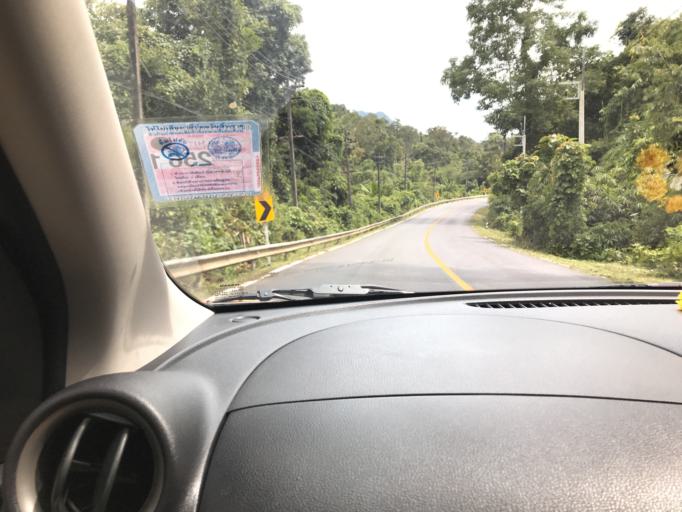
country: TH
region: Kanchanaburi
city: Sangkhla Buri
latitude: 15.1377
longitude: 98.5090
